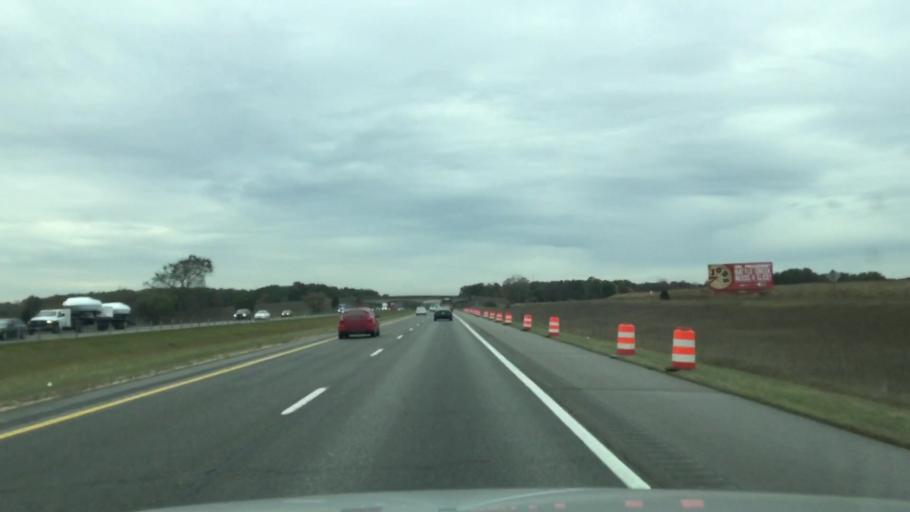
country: US
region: Michigan
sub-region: Calhoun County
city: Marshall
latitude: 42.2977
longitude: -85.0255
